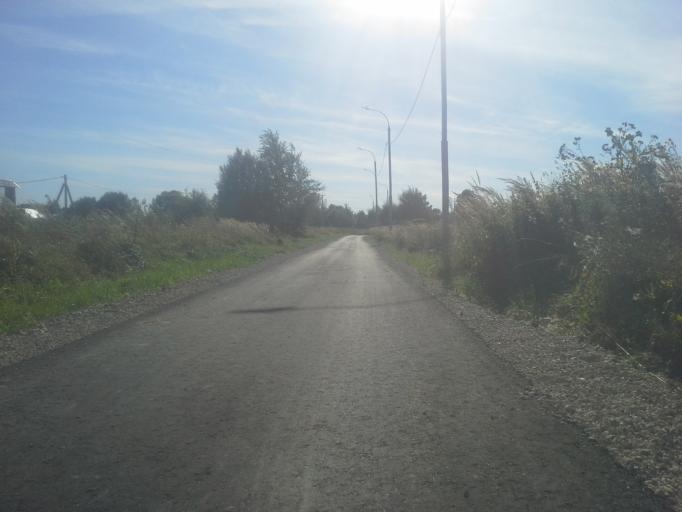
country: RU
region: Moskovskaya
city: Aprelevka
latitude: 55.4384
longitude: 37.0697
